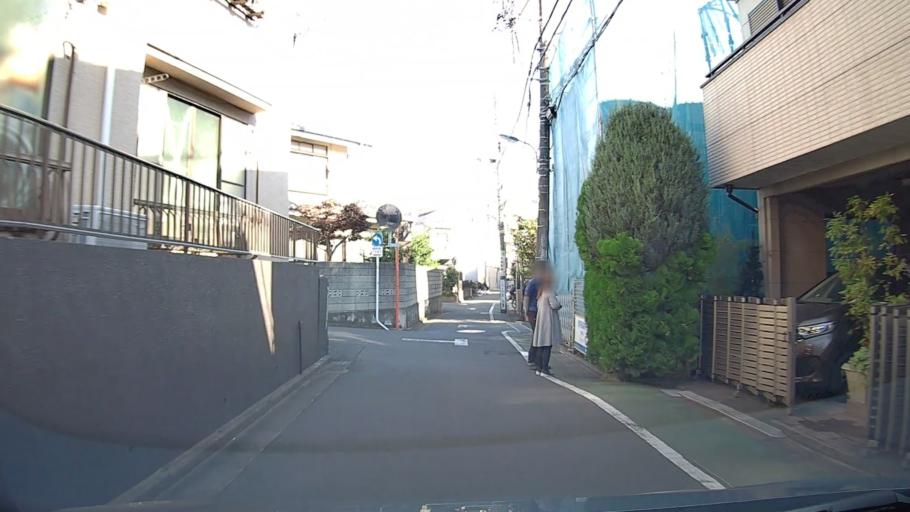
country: JP
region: Saitama
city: Wako
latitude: 35.7384
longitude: 139.6294
